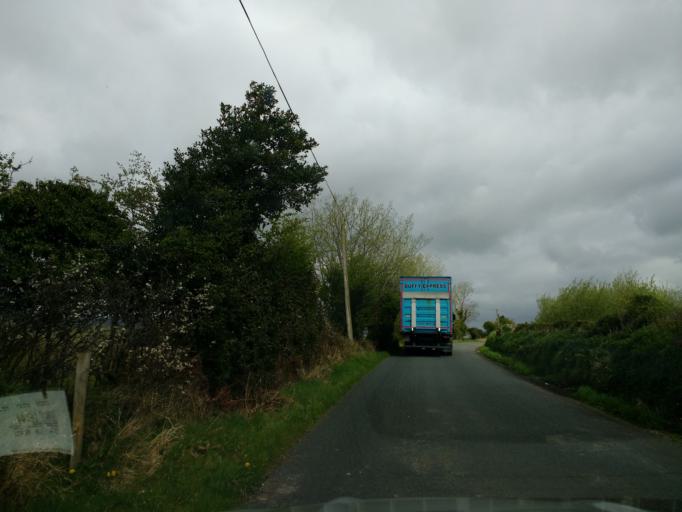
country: IE
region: Ulster
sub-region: County Donegal
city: Ramelton
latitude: 55.0712
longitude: -7.6138
